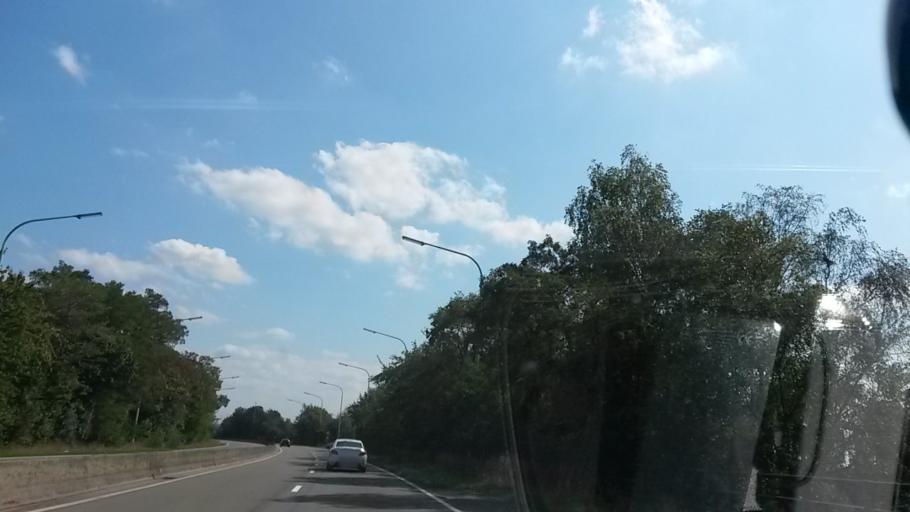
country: BE
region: Wallonia
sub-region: Province de Namur
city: Fosses-la-Ville
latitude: 50.4289
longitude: 4.7095
